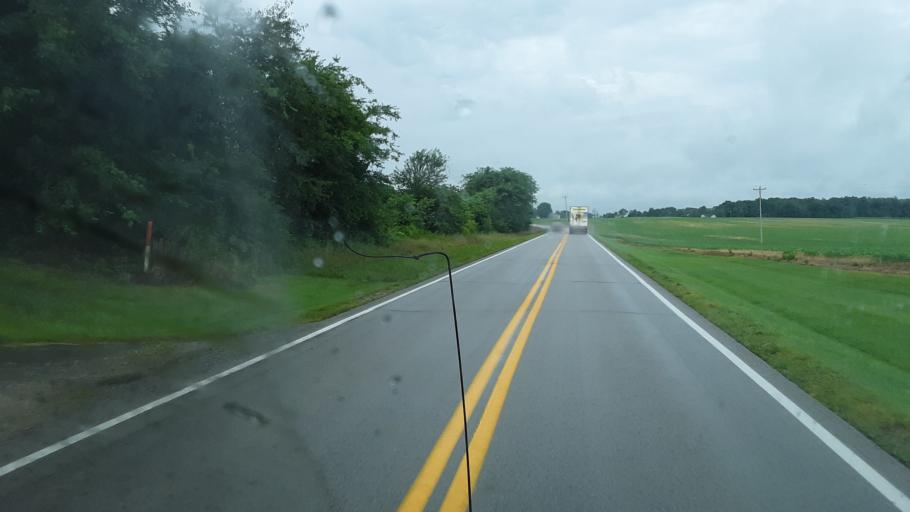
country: US
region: Kentucky
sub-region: Logan County
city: Russellville
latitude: 36.7797
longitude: -87.0036
